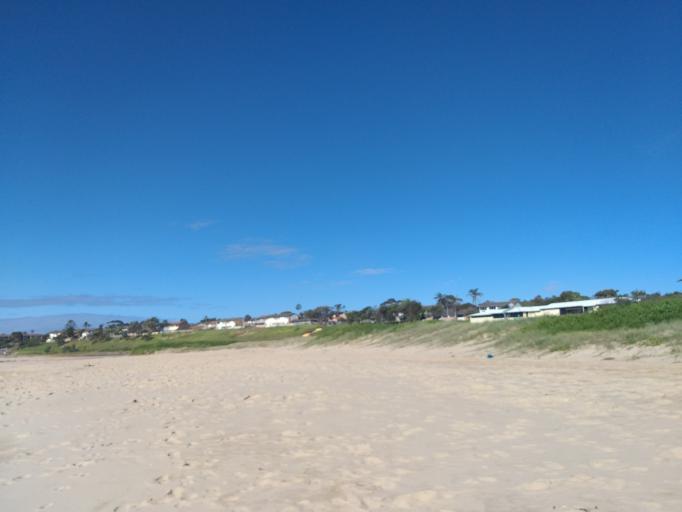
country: AU
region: New South Wales
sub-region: Wollongong
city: East Corrimal
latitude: -34.3631
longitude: 150.9208
